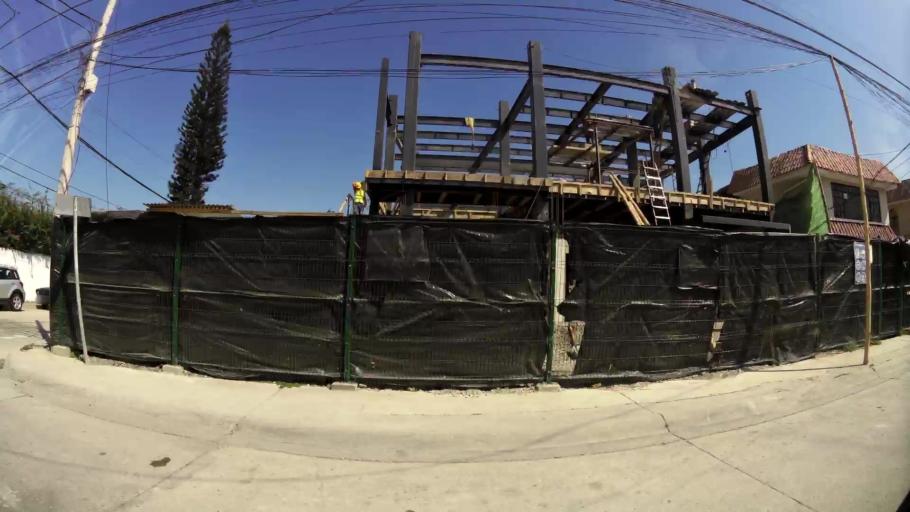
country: EC
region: Guayas
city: Guayaquil
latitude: -2.1757
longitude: -79.9071
